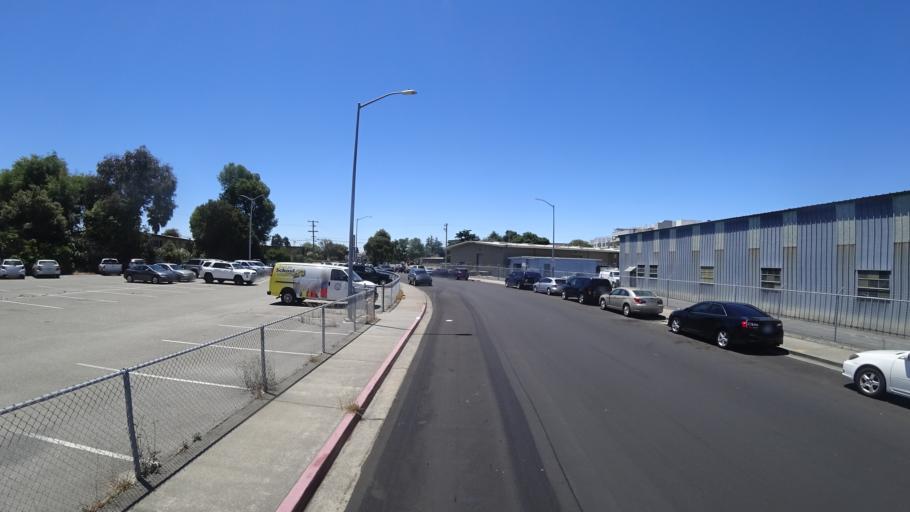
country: US
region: California
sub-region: Alameda County
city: Hayward
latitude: 37.6571
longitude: -122.0920
